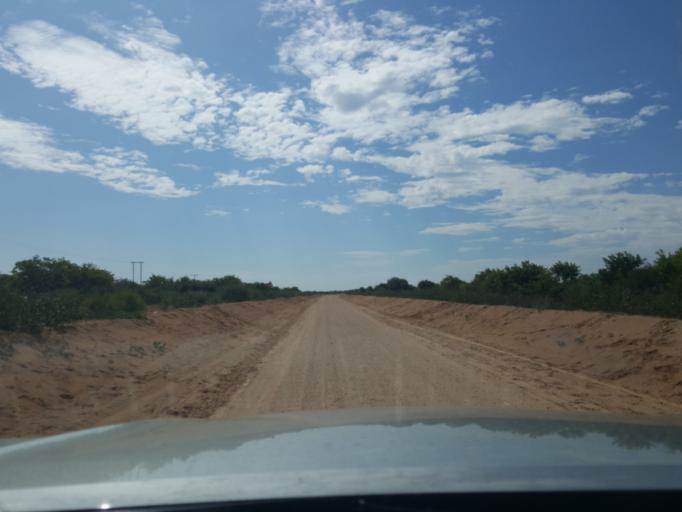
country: BW
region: Kweneng
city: Khudumelapye
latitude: -23.8550
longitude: 24.8769
